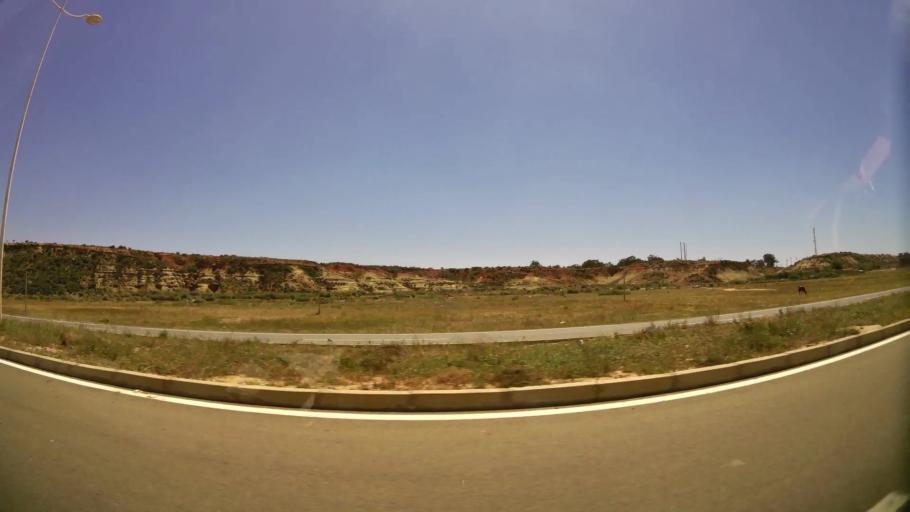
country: MA
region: Oriental
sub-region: Berkane-Taourirt
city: Madagh
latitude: 35.0982
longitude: -2.3213
